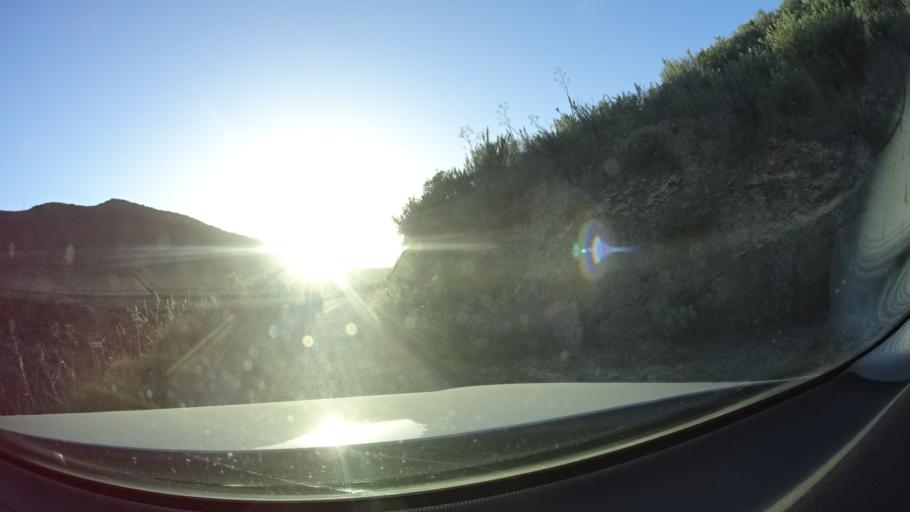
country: ES
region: Canary Islands
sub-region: Provincia de Las Palmas
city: Artenara
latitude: 28.0363
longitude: -15.6455
